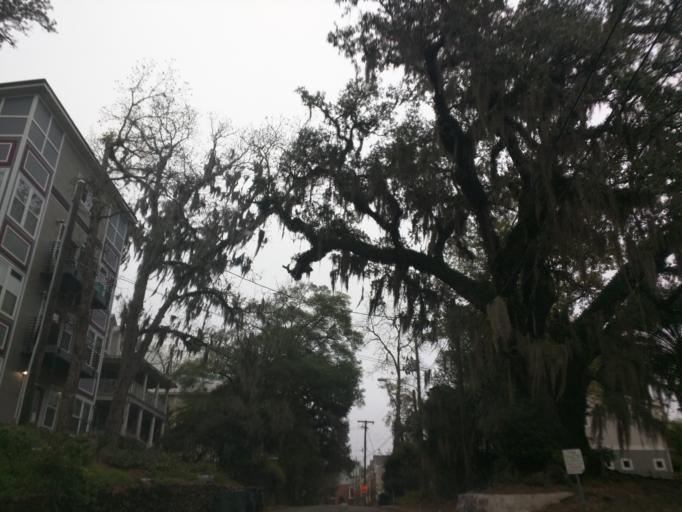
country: US
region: Florida
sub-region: Leon County
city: Tallahassee
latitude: 30.4344
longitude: -84.2882
